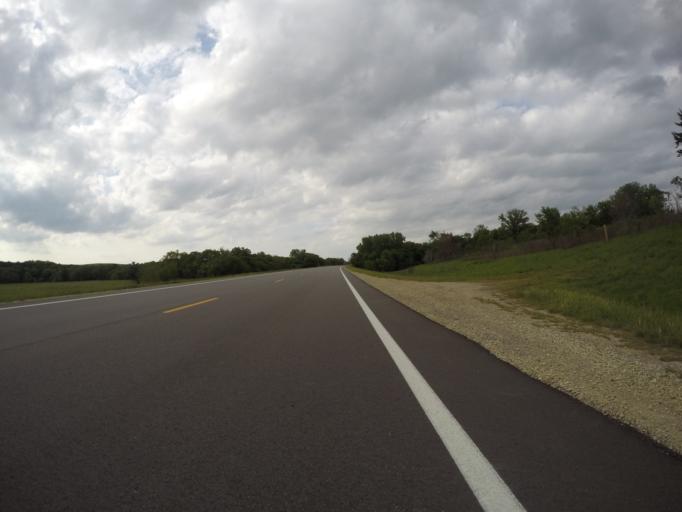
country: US
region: Kansas
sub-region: Riley County
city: Manhattan
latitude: 39.2815
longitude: -96.5582
